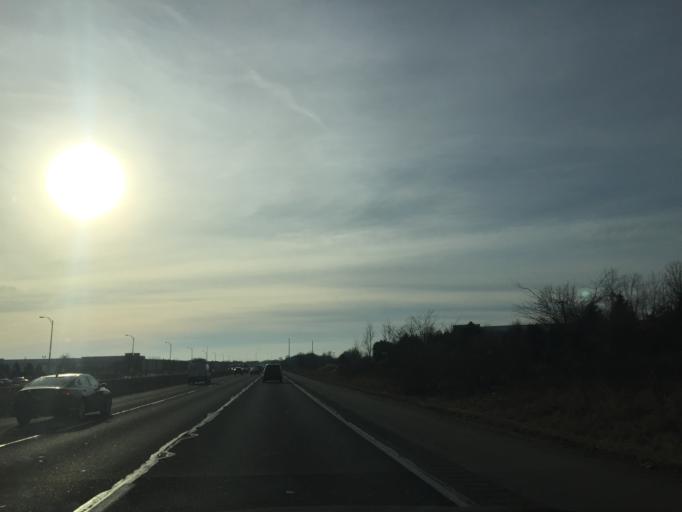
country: US
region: Illinois
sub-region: Will County
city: Romeoville
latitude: 41.6485
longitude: -88.1401
